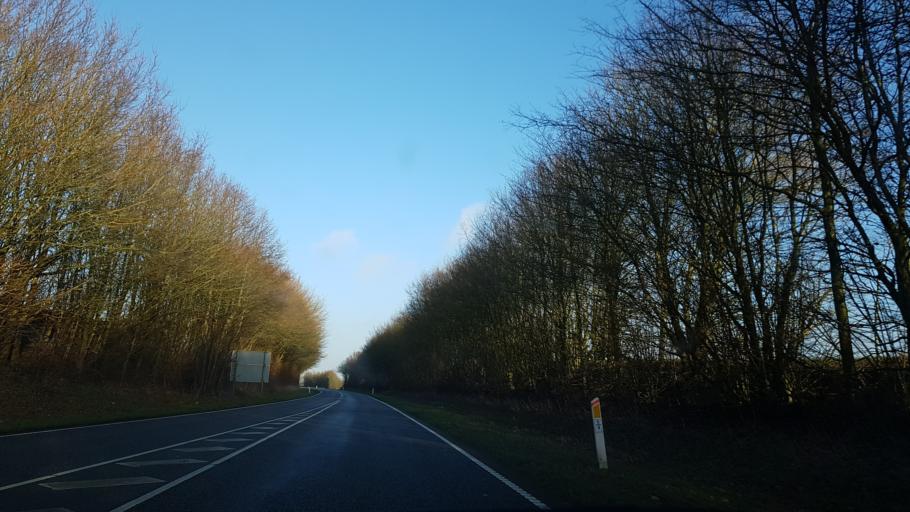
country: DK
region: South Denmark
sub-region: Haderslev Kommune
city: Haderslev
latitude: 55.2032
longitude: 9.4535
